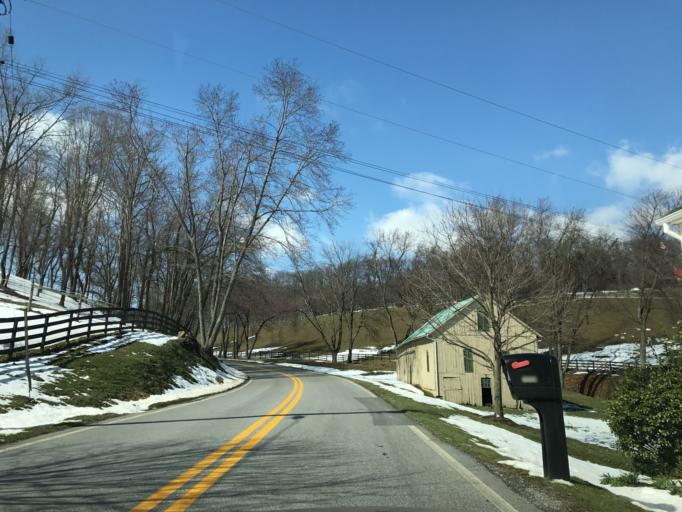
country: US
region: Maryland
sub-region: Carroll County
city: Manchester
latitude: 39.7182
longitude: -76.8499
